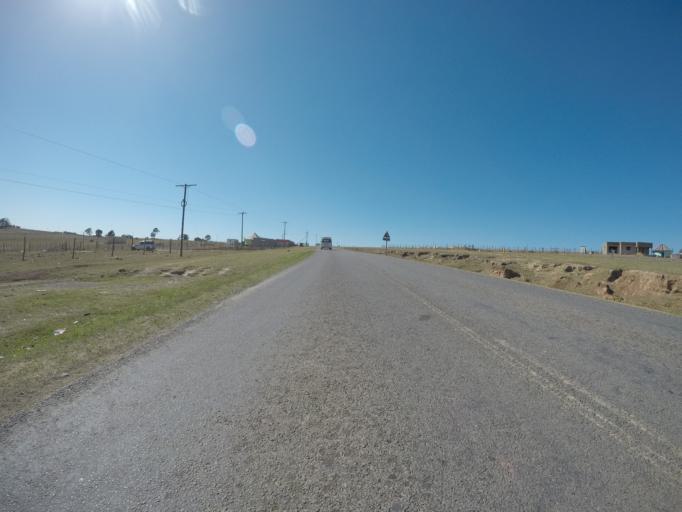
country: ZA
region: Eastern Cape
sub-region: OR Tambo District Municipality
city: Mthatha
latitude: -31.8829
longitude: 28.7568
